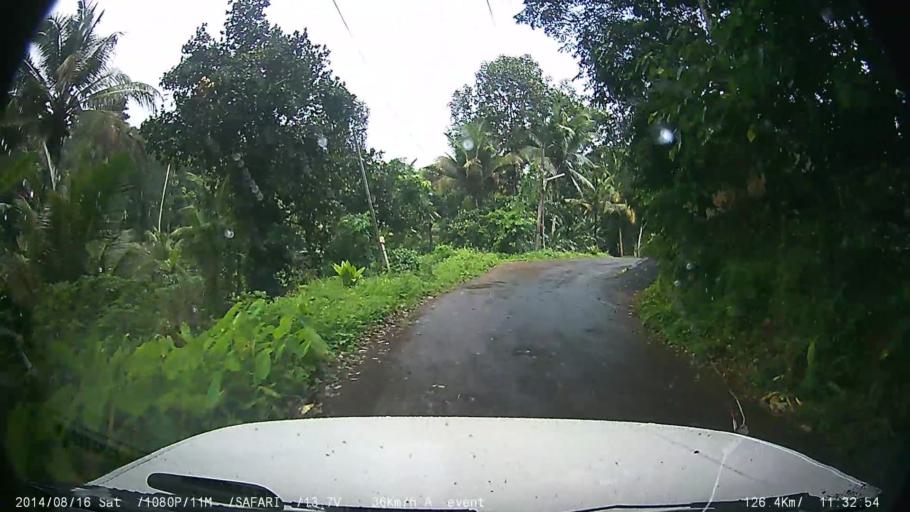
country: IN
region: Kerala
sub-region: Kottayam
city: Palackattumala
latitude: 9.7738
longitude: 76.5579
